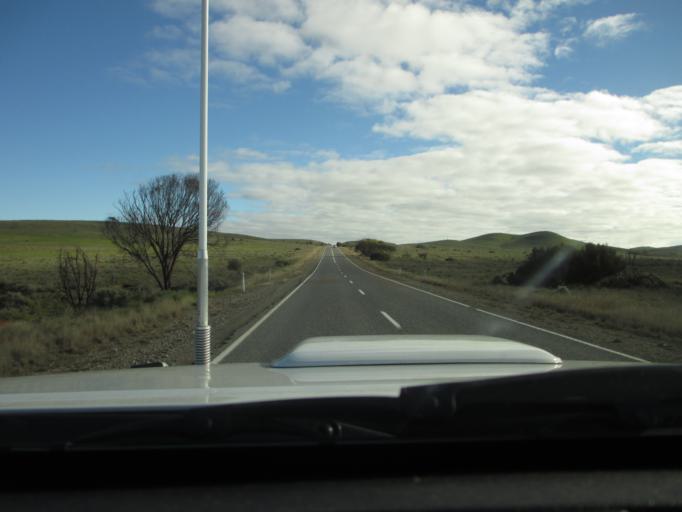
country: AU
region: South Australia
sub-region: Peterborough
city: Peterborough
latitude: -32.6184
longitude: 138.5768
